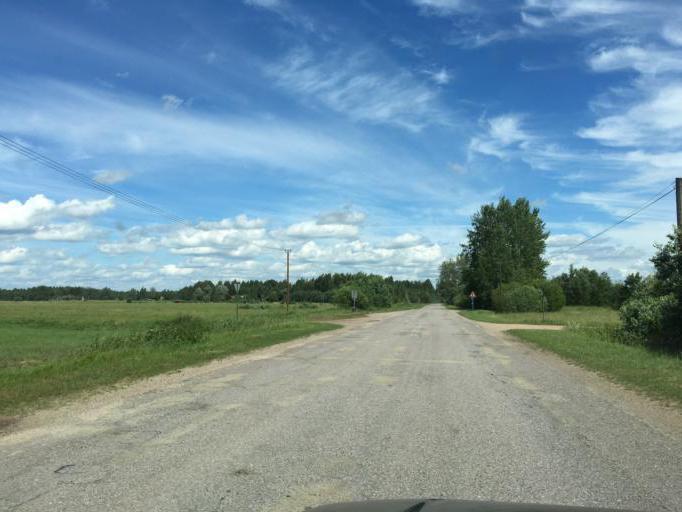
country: LV
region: Balvu Rajons
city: Balvi
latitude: 57.1563
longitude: 27.3165
